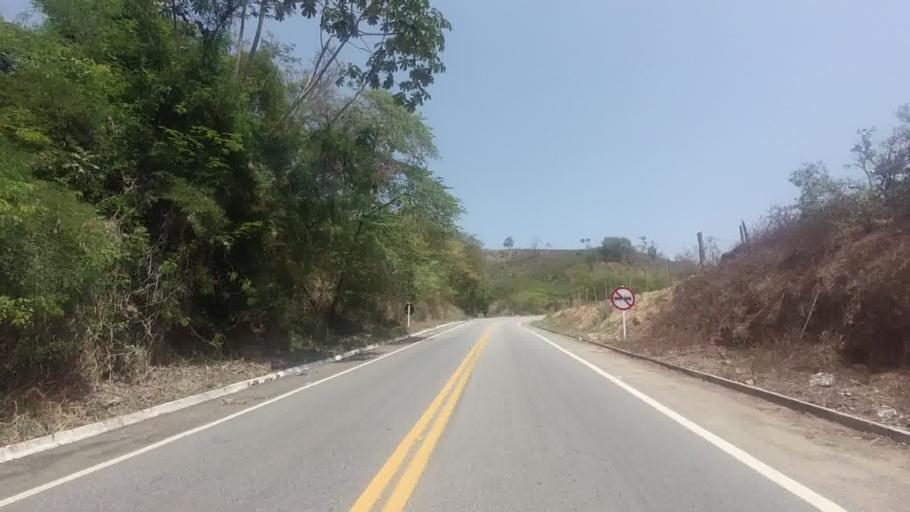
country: BR
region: Espirito Santo
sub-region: Cachoeiro De Itapemirim
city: Cachoeiro de Itapemirim
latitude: -20.8385
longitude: -41.2311
